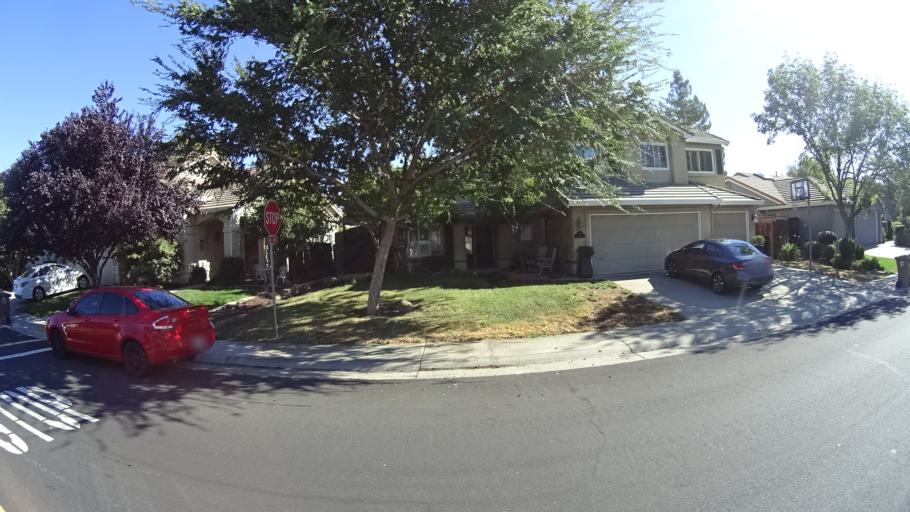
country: US
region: California
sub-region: Sacramento County
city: Elk Grove
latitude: 38.4183
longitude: -121.3650
